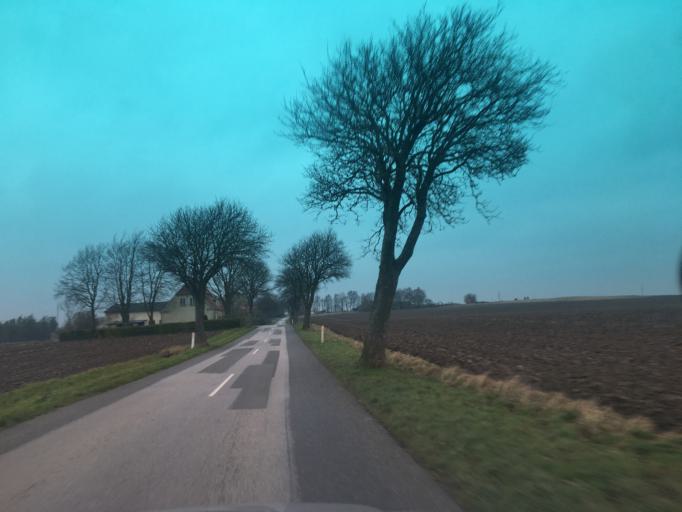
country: DK
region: Zealand
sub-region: Slagelse Kommune
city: Skaelskor
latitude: 55.2432
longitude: 11.4236
